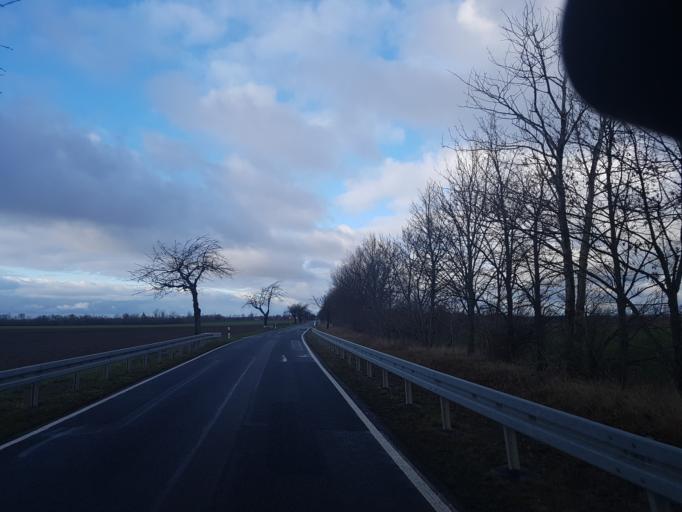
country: DE
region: Brandenburg
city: Muhlberg
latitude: 51.4191
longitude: 13.2323
